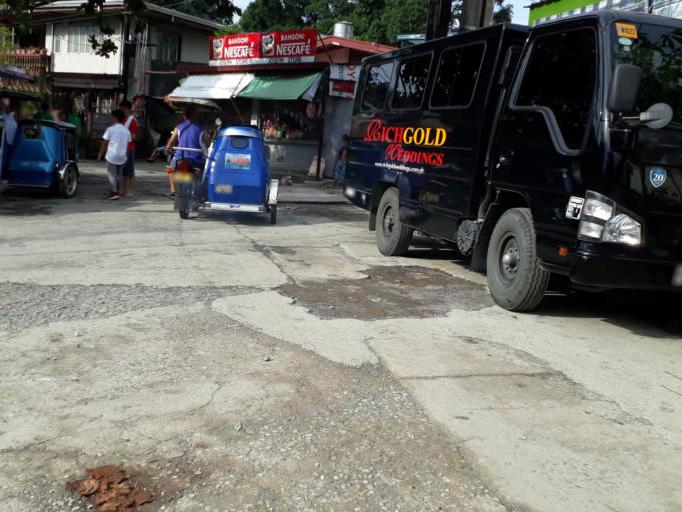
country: PH
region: Calabarzon
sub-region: Province of Rizal
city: Valenzuela
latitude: 14.6754
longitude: 120.9908
